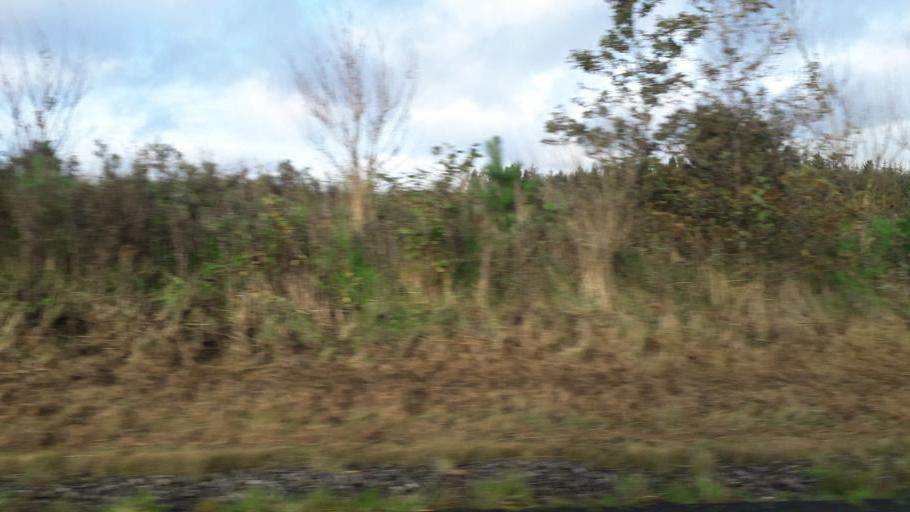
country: IE
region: Connaught
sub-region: Roscommon
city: Ballaghaderreen
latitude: 53.8916
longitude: -8.5042
